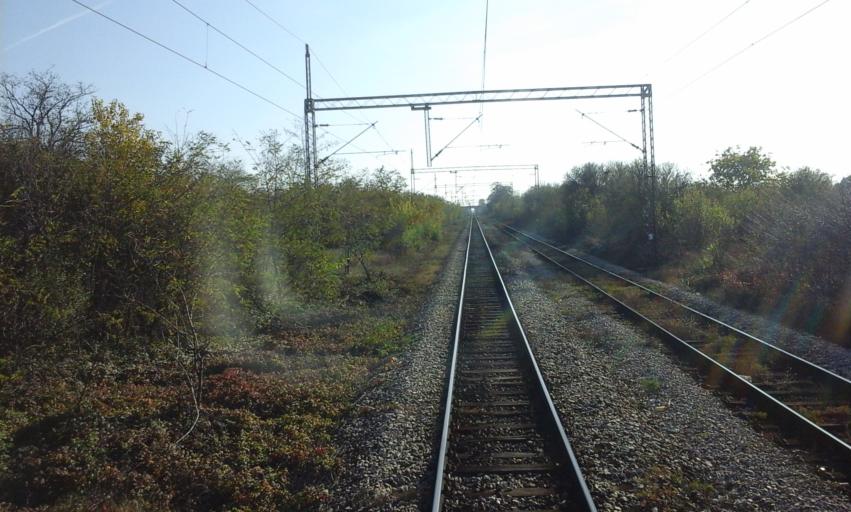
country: RS
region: Autonomna Pokrajina Vojvodina
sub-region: Severnobacki Okrug
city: Mali Igos
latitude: 45.7498
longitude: 19.6488
